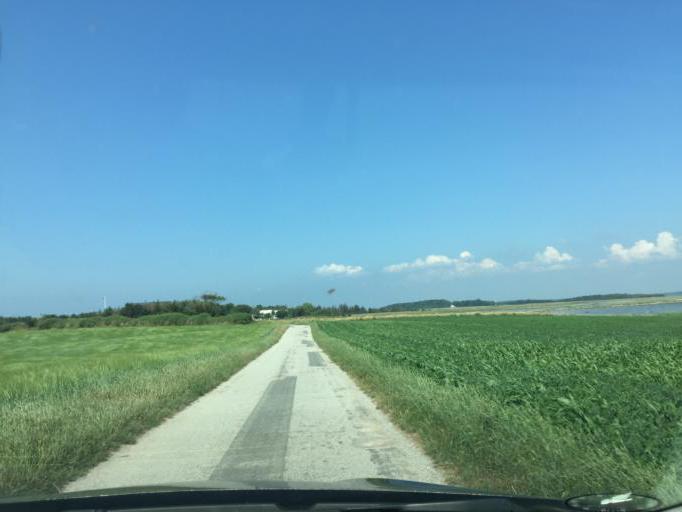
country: DK
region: Zealand
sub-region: Slagelse Kommune
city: Korsor
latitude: 55.2285
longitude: 11.1781
